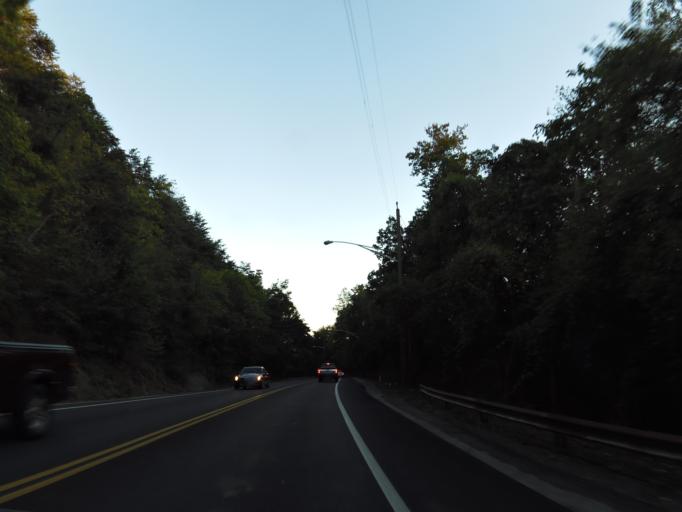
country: US
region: Tennessee
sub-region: Knox County
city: Knoxville
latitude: 35.9978
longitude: -83.9534
